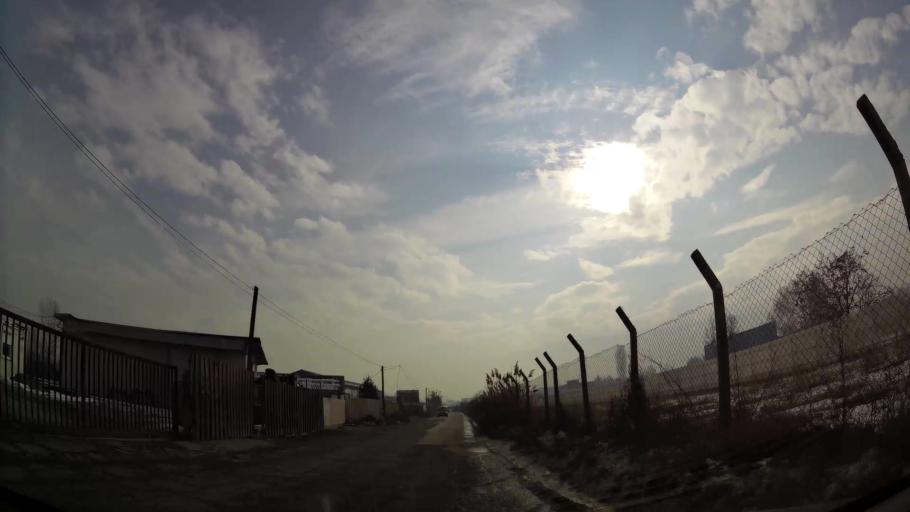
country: MK
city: Krushopek
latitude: 42.0167
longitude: 21.3681
